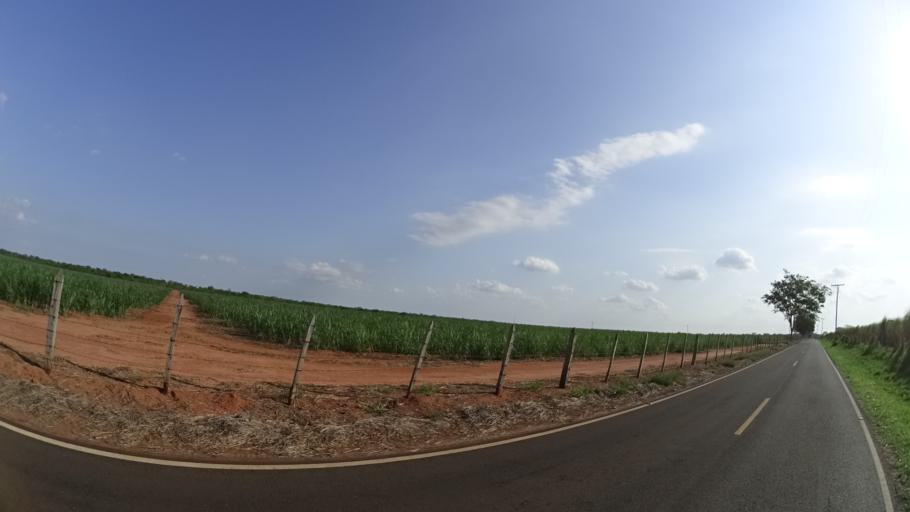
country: BR
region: Sao Paulo
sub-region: Urupes
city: Urupes
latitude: -21.3879
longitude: -49.4993
